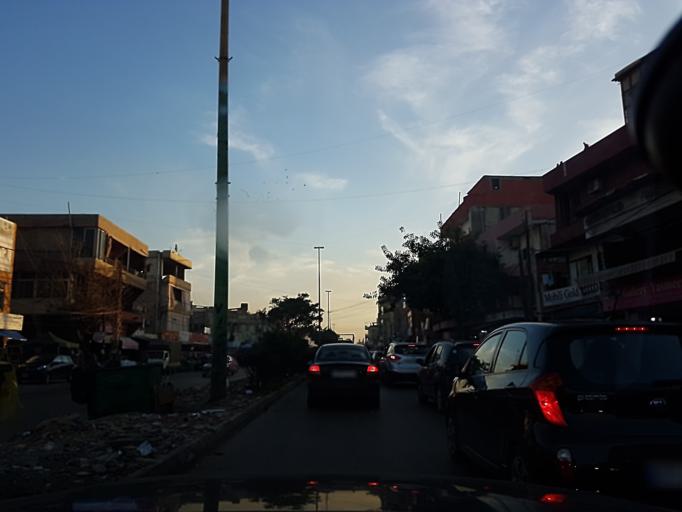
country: LB
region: Beyrouth
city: Beirut
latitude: 33.8485
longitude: 35.4851
